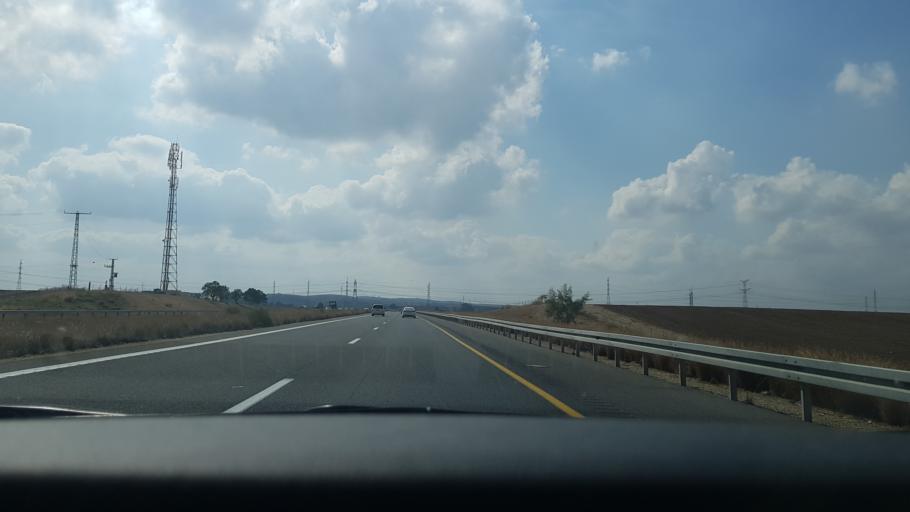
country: IL
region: Central District
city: Bene 'Ayish
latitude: 31.7192
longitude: 34.8204
